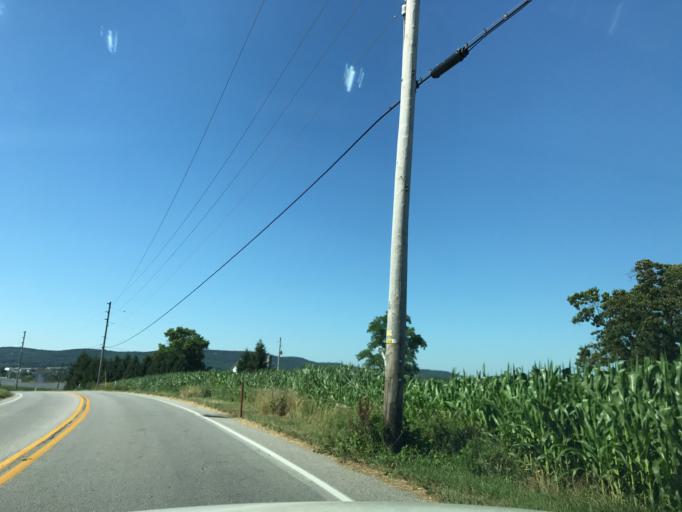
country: US
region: Pennsylvania
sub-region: York County
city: Parkville
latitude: 39.8058
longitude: -76.9444
